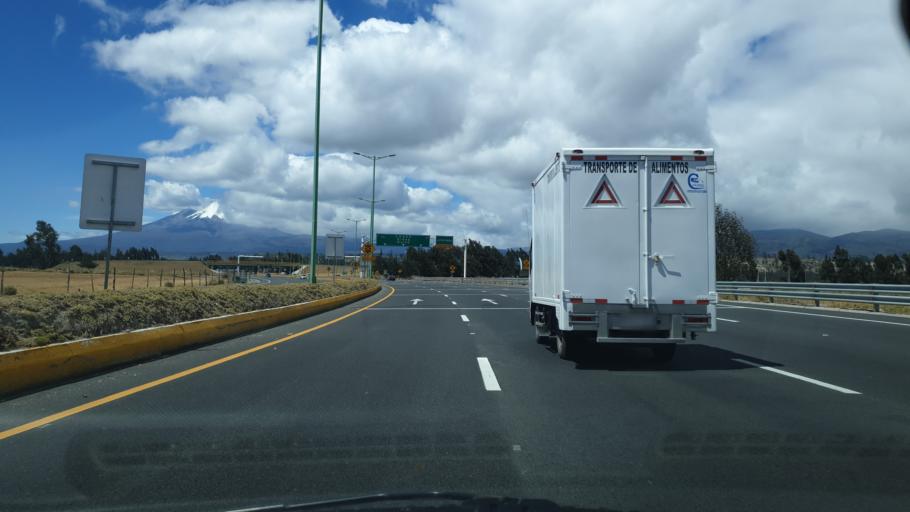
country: EC
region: Cotopaxi
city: Saquisili
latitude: -0.8682
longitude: -78.6305
